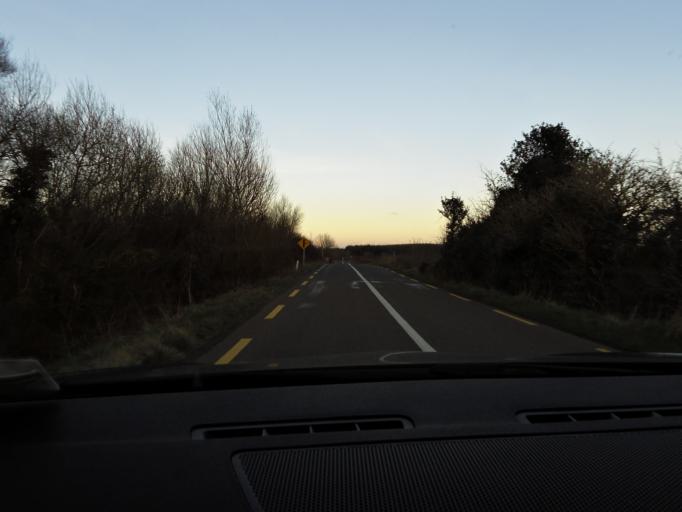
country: IE
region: Connaught
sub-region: Roscommon
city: Boyle
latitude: 53.9737
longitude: -8.4354
